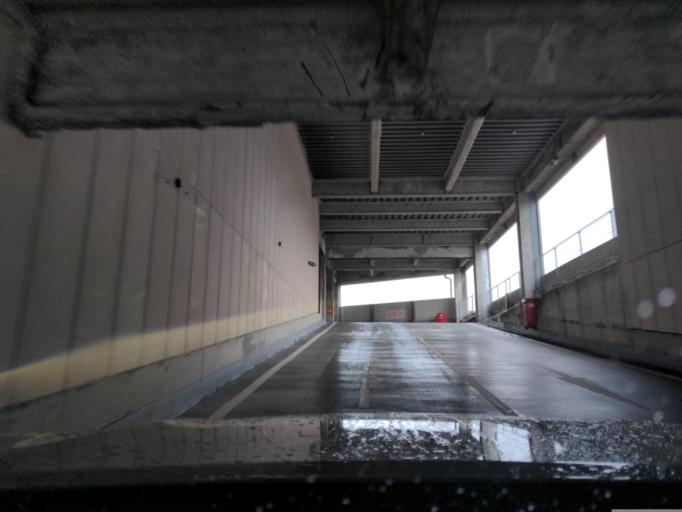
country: JP
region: Niigata
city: Kashiwazaki
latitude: 37.3697
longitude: 138.5569
